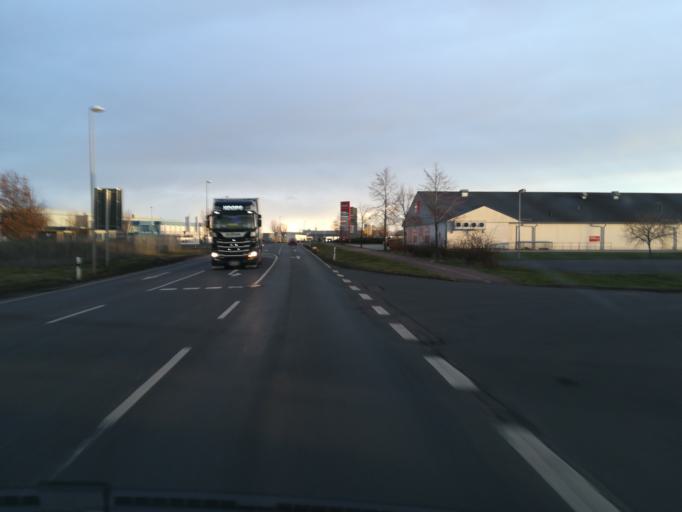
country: DE
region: Saxony-Anhalt
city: Landsberg
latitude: 51.5386
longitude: 12.1577
